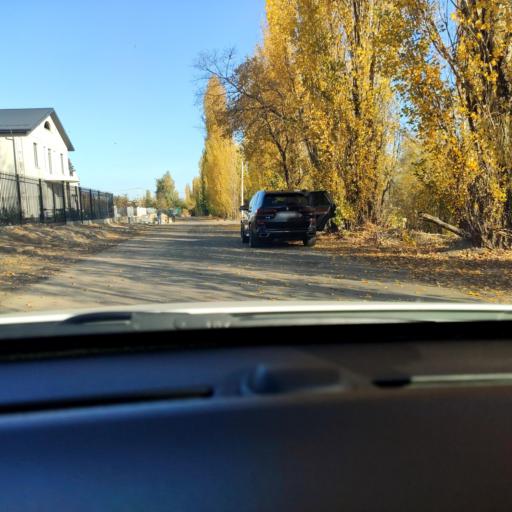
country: RU
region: Voronezj
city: Voronezh
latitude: 51.7061
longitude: 39.2387
